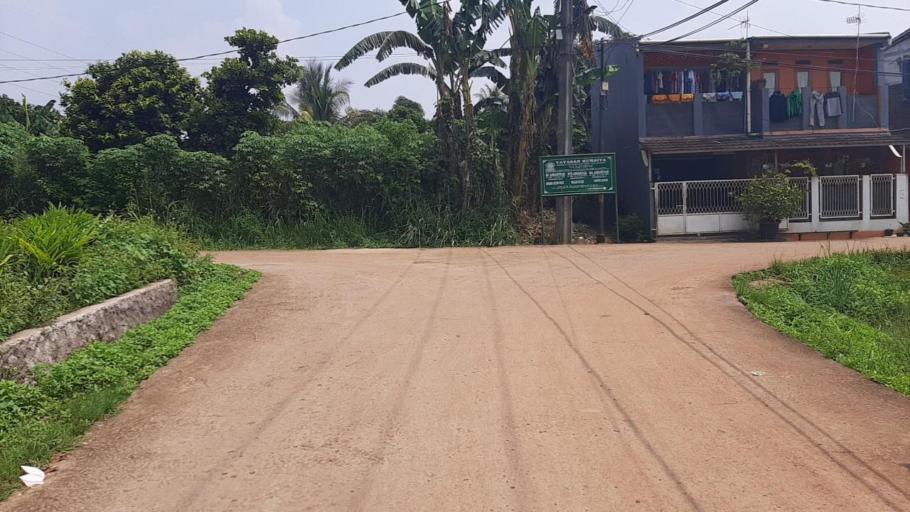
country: ID
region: West Java
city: Cileungsir
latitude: -6.4221
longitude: 106.9132
